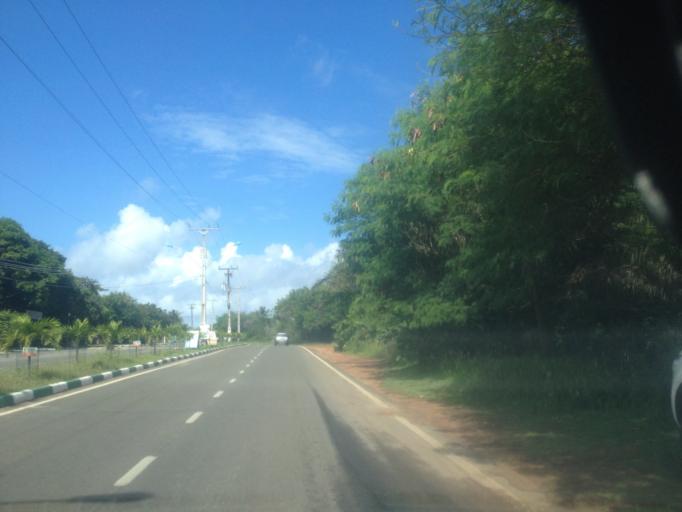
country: BR
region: Bahia
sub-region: Mata De Sao Joao
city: Mata de Sao Joao
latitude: -12.6485
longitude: -38.0736
